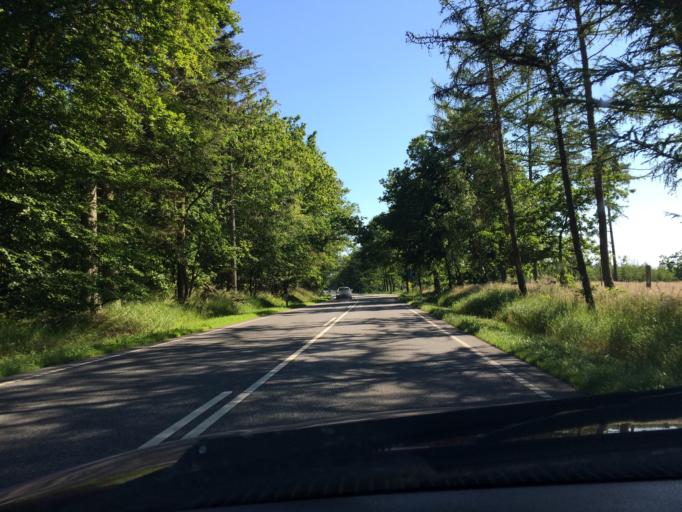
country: DK
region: Central Jutland
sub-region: Viborg Kommune
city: Bjerringbro
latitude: 56.3068
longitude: 9.6863
